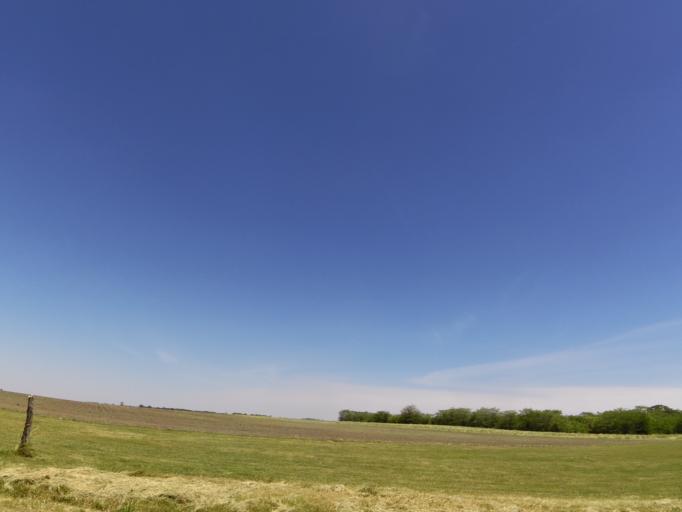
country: US
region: Illinois
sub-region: Iroquois County
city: Milford
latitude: 40.6319
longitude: -87.7336
